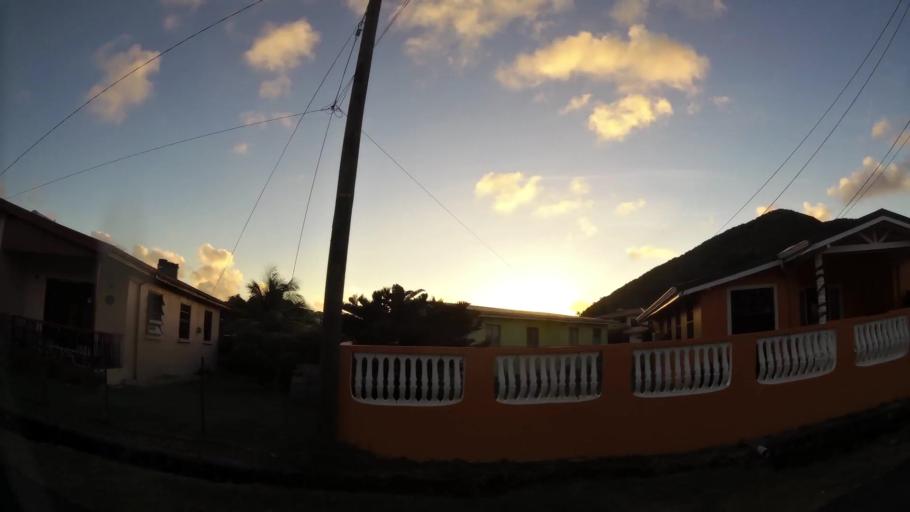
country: LC
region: Gros-Islet
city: Gros Islet
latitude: 14.0666
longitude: -60.9548
